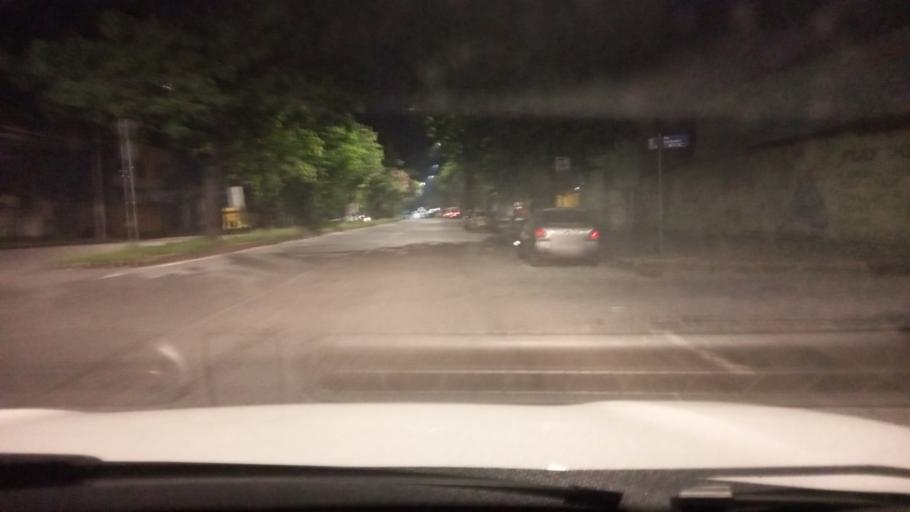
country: BR
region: Minas Gerais
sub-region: Belo Horizonte
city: Belo Horizonte
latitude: -19.8933
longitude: -43.9591
